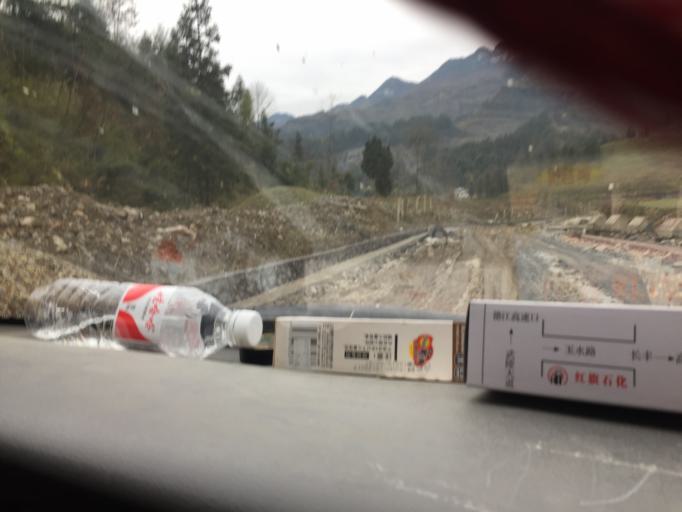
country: CN
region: Guizhou Sheng
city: Changfeng
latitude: 28.4302
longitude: 108.0806
